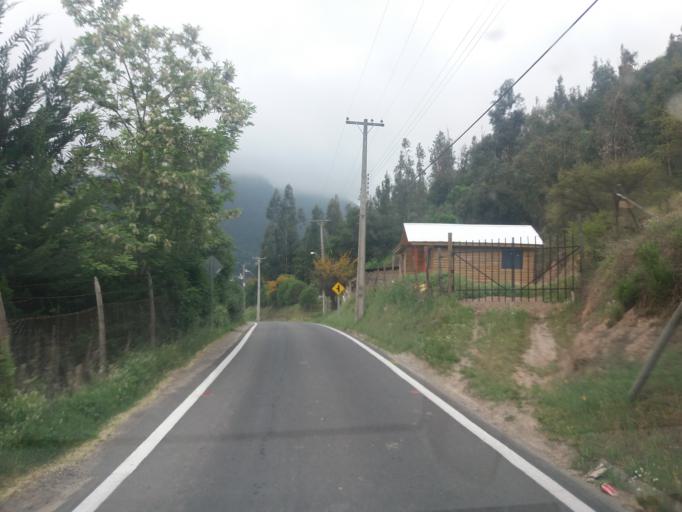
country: CL
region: Valparaiso
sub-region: Provincia de Marga Marga
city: Limache
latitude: -33.0461
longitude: -71.0995
